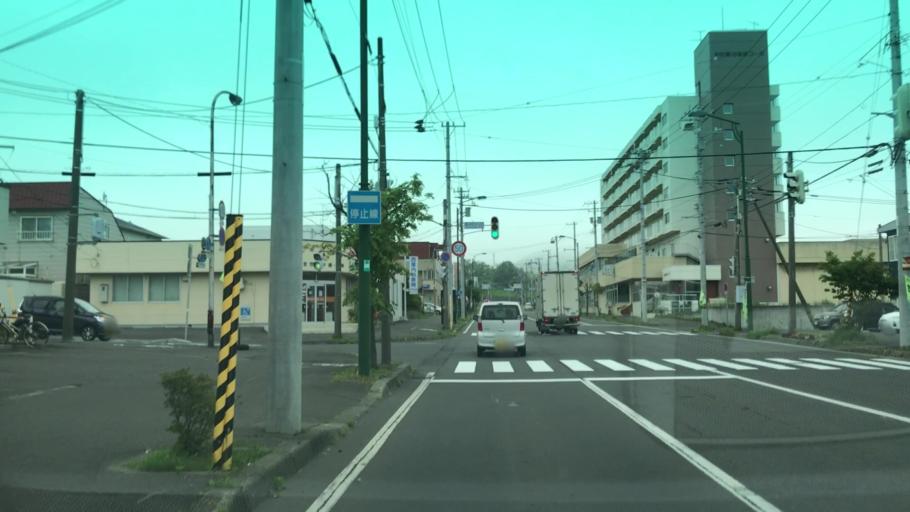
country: JP
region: Hokkaido
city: Muroran
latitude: 42.3630
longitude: 141.0391
